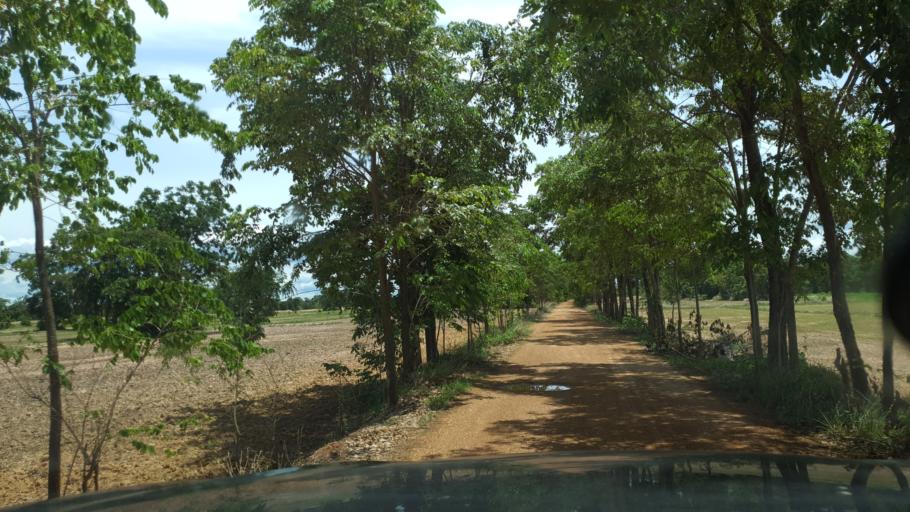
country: TH
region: Sukhothai
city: Ban Na
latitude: 17.1412
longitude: 99.6692
